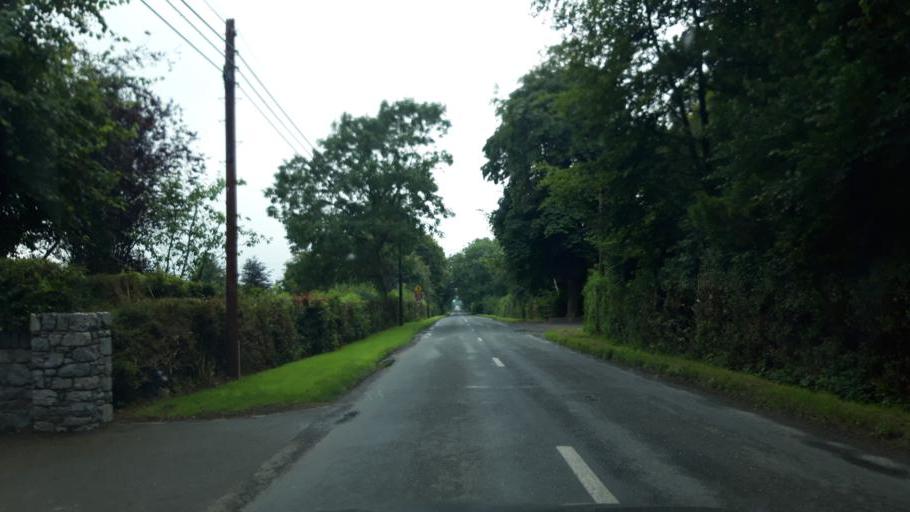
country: IE
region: Munster
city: Fethard
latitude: 52.5018
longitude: -7.6864
